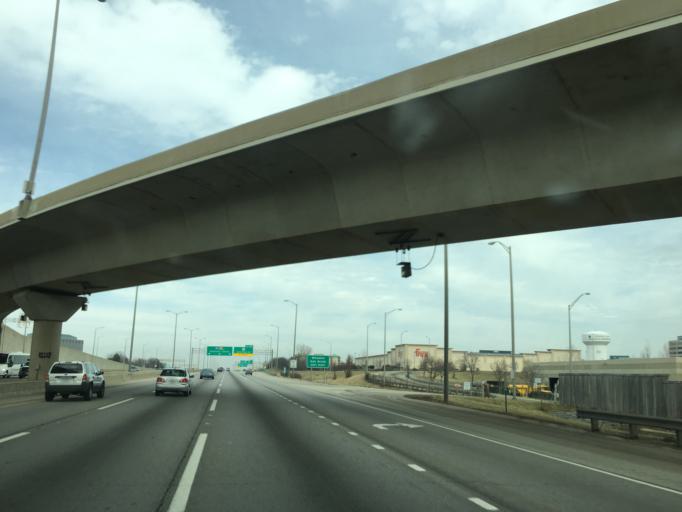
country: US
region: Illinois
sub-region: DuPage County
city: Downers Grove
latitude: 41.8224
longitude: -88.0282
